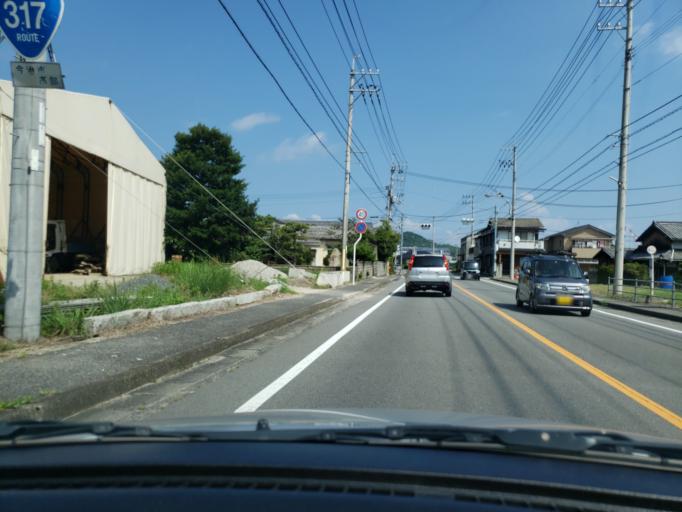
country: JP
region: Ehime
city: Hojo
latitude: 34.0970
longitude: 132.9729
